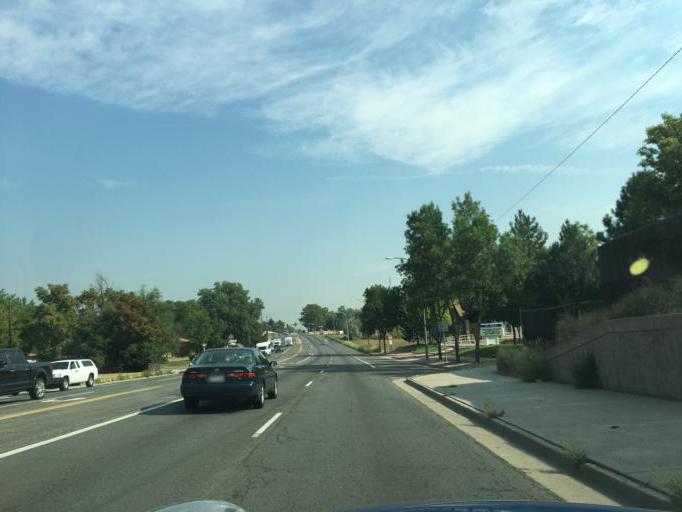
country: US
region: Colorado
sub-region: Jefferson County
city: Wheat Ridge
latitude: 39.7518
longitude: -105.0813
